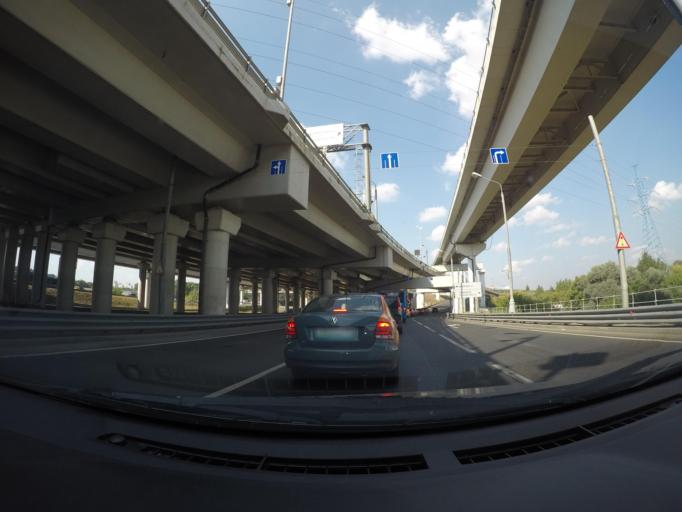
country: RU
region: Moskovskaya
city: Levoberezhnaya
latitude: 55.8829
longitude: 37.4831
